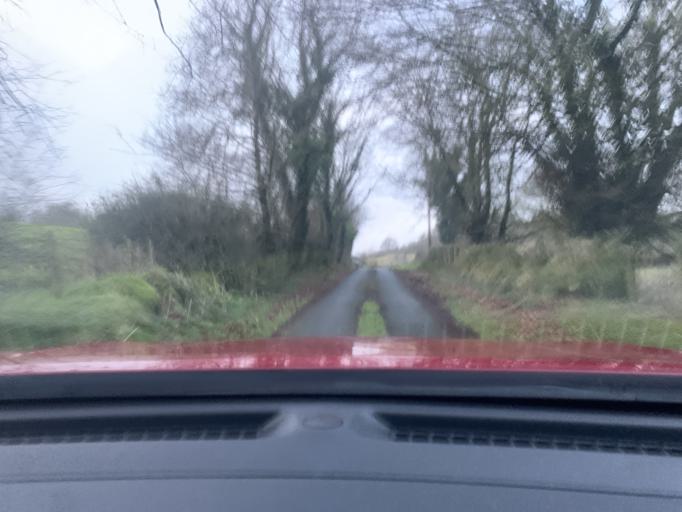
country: IE
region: Connaught
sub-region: Sligo
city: Ballymote
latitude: 54.0419
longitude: -8.4092
